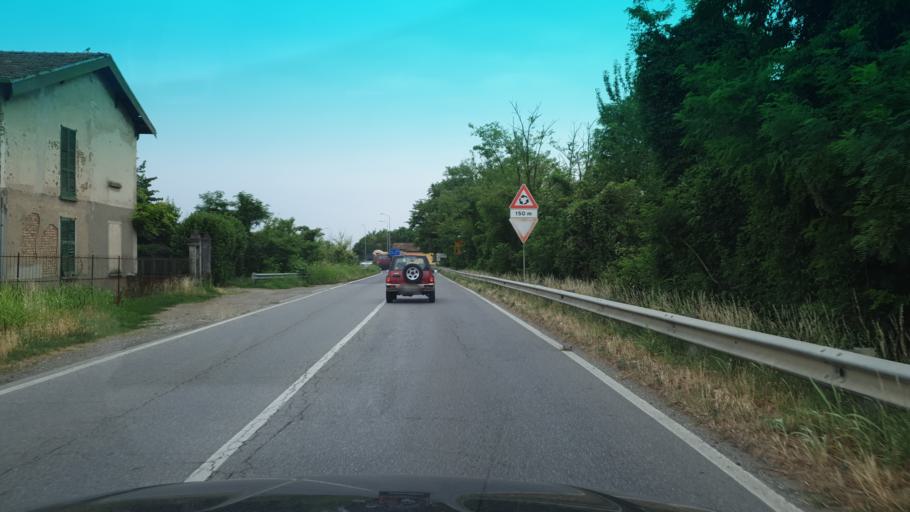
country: IT
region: Lombardy
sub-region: Citta metropolitana di Milano
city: Cassano d'Adda
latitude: 45.5269
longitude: 9.5365
